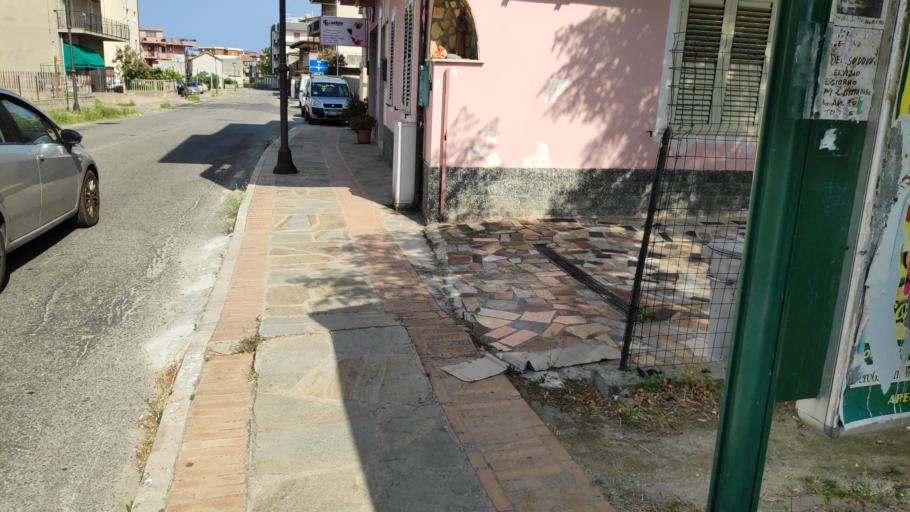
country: IT
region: Calabria
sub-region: Provincia di Catanzaro
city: Marina di Davoli
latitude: 38.6676
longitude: 16.5424
